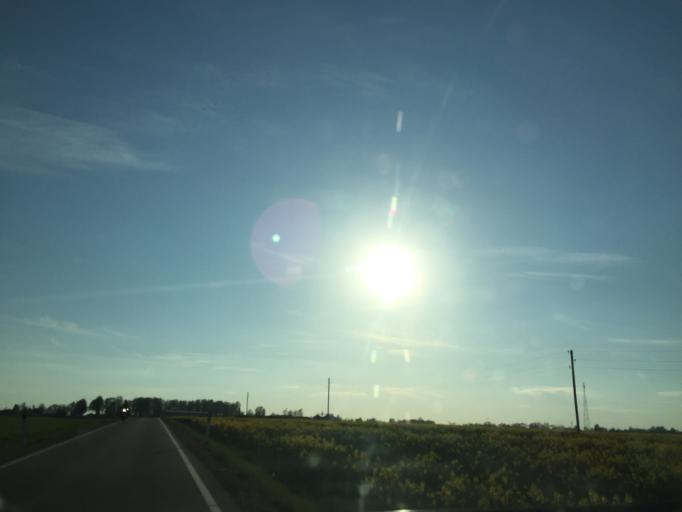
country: LV
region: Bauskas Rajons
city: Bauska
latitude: 56.3097
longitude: 24.2739
